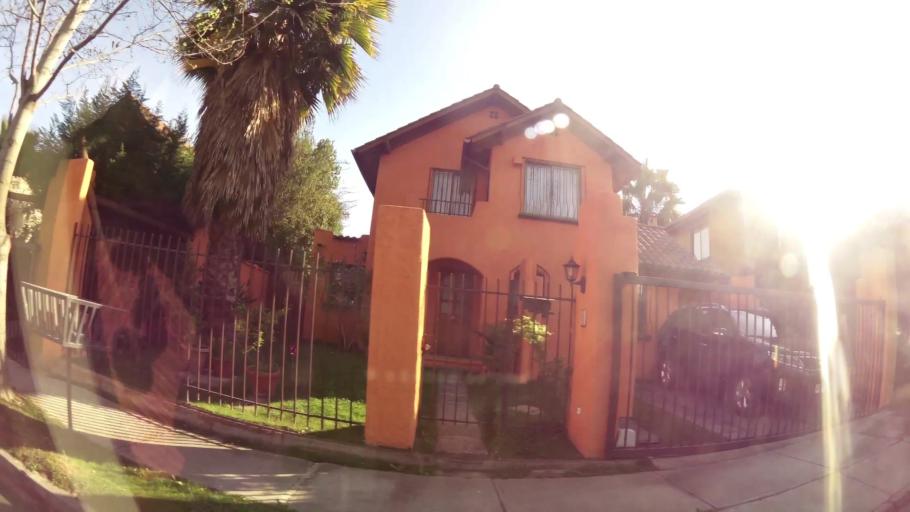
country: CL
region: Santiago Metropolitan
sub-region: Provincia de Santiago
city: Villa Presidente Frei, Nunoa, Santiago, Chile
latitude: -33.4849
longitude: -70.5504
